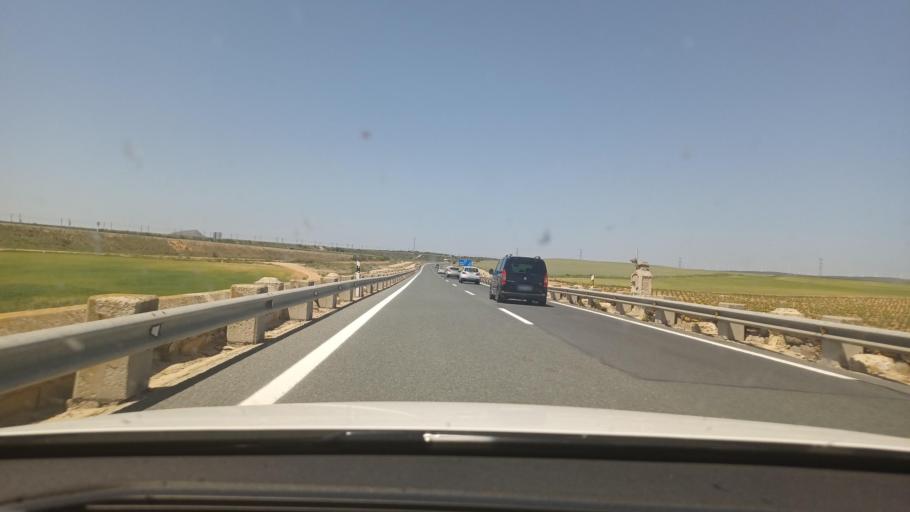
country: ES
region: Castille-La Mancha
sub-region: Provincia de Albacete
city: Alpera
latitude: 38.8784
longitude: -1.2300
